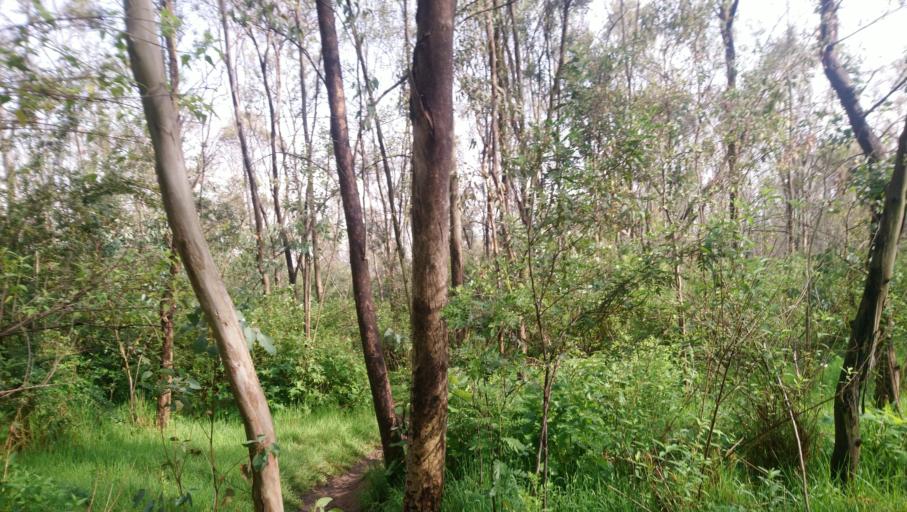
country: MX
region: Mexico
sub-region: Tultitlan
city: Ampliacion San Mateo (Colonia Solidaridad)
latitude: 19.6072
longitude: -99.1227
